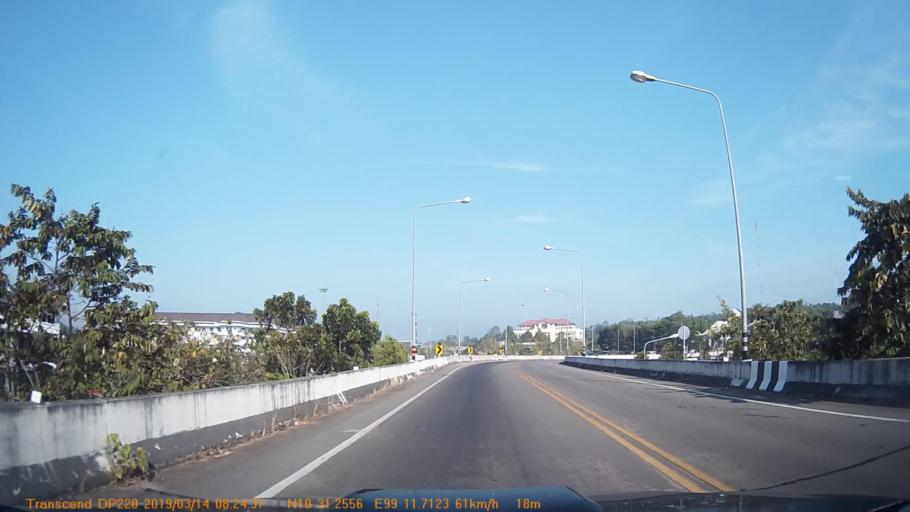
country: TH
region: Chumphon
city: Chumphon
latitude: 10.5210
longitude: 99.1951
